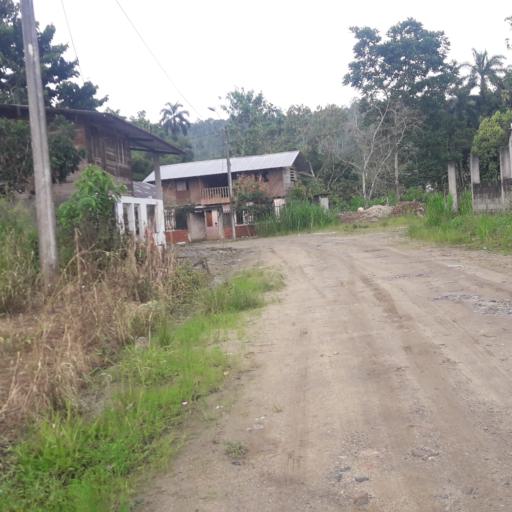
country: EC
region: Napo
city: Tena
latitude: -0.9909
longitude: -77.8108
